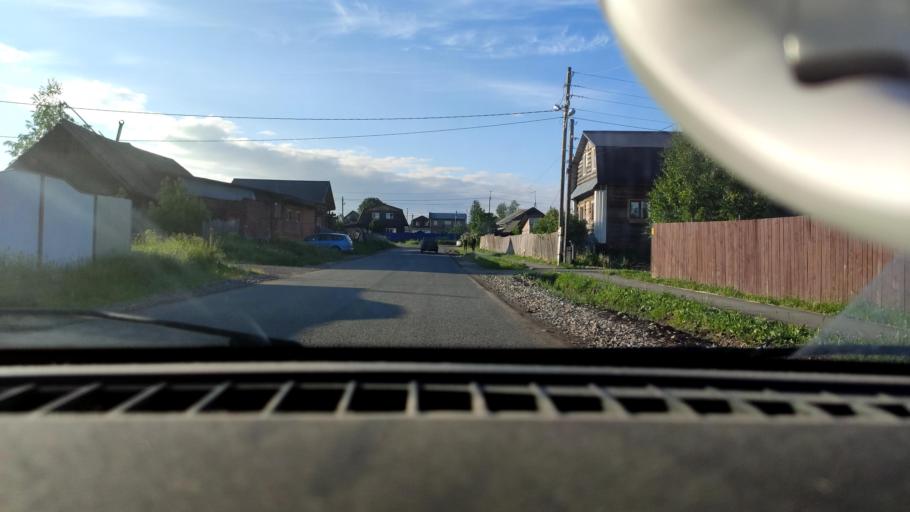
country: RU
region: Perm
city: Novyye Lyady
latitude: 58.0533
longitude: 56.6002
